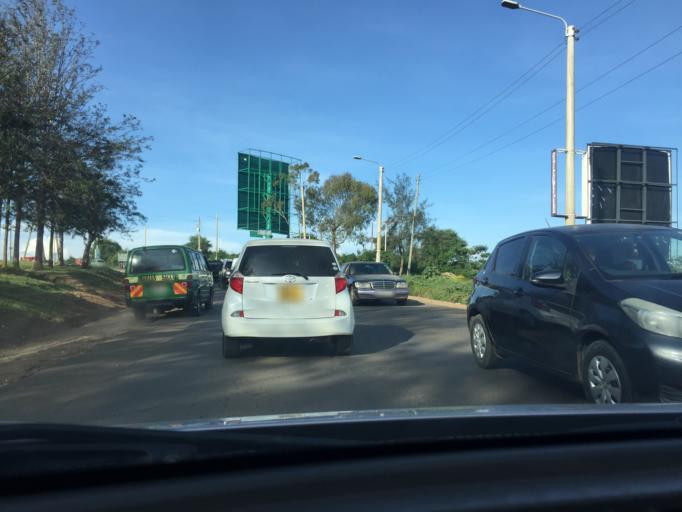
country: KE
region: Nairobi Area
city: Nairobi
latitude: -1.3872
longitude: 36.7707
